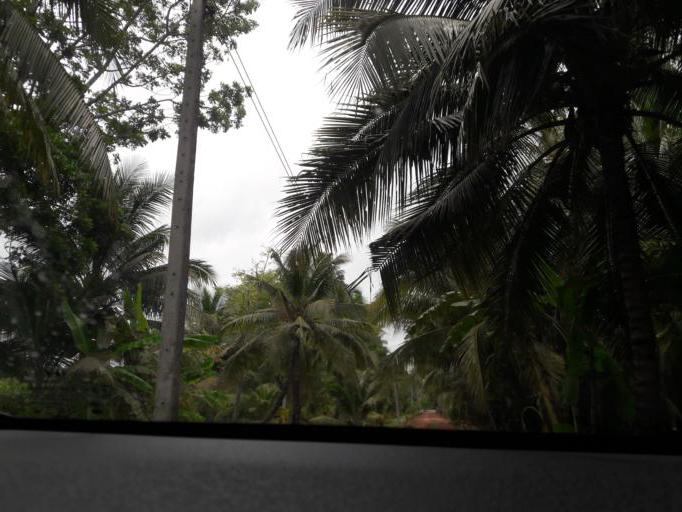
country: TH
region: Ratchaburi
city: Damnoen Saduak
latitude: 13.5729
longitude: 99.9889
